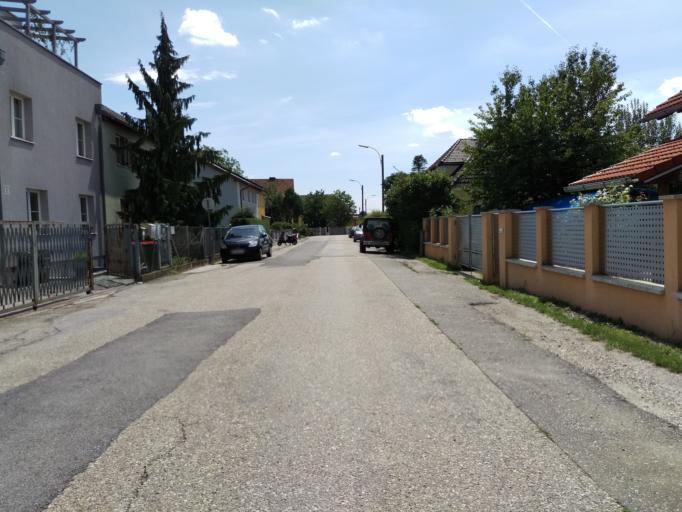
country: AT
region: Styria
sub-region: Graz Stadt
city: Wetzelsdorf
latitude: 47.0567
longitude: 15.4184
